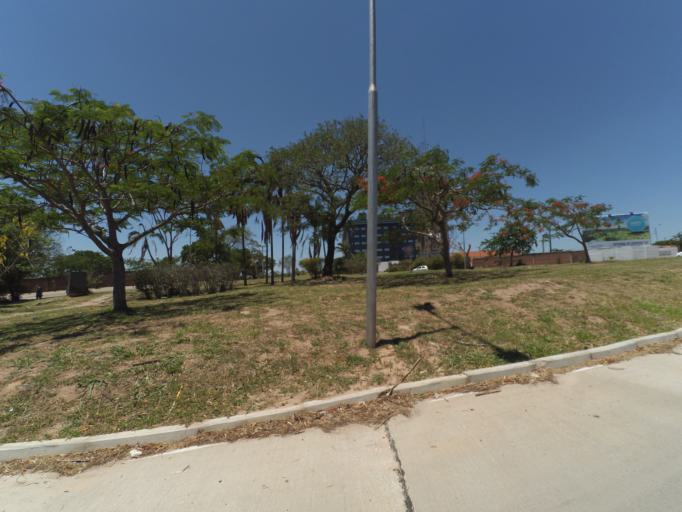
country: BO
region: Santa Cruz
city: Santa Cruz de la Sierra
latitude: -17.7495
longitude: -63.2162
